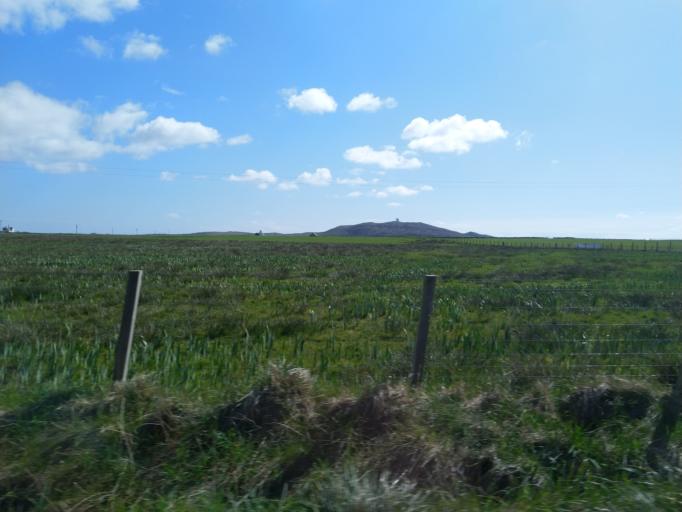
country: GB
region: Scotland
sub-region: Eilean Siar
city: Barra
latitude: 56.4836
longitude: -6.9105
